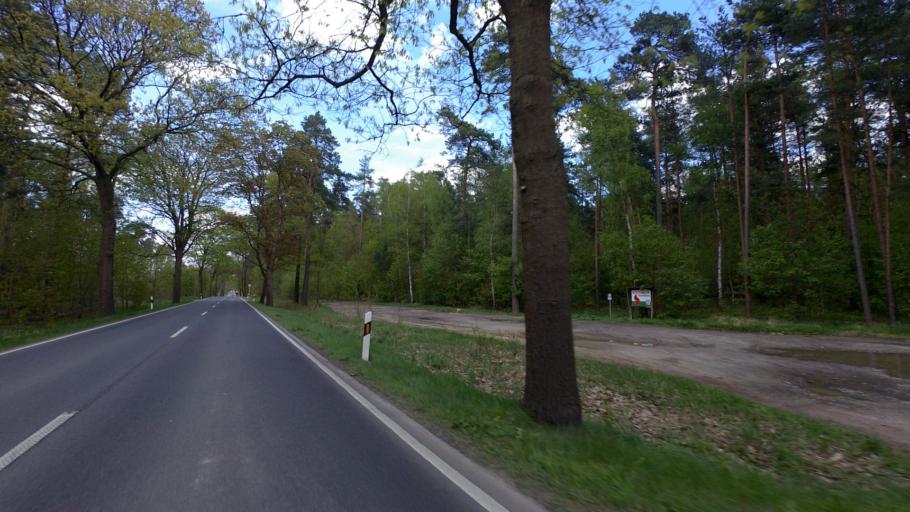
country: DE
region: Brandenburg
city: Marienwerder
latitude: 52.9757
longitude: 13.5795
